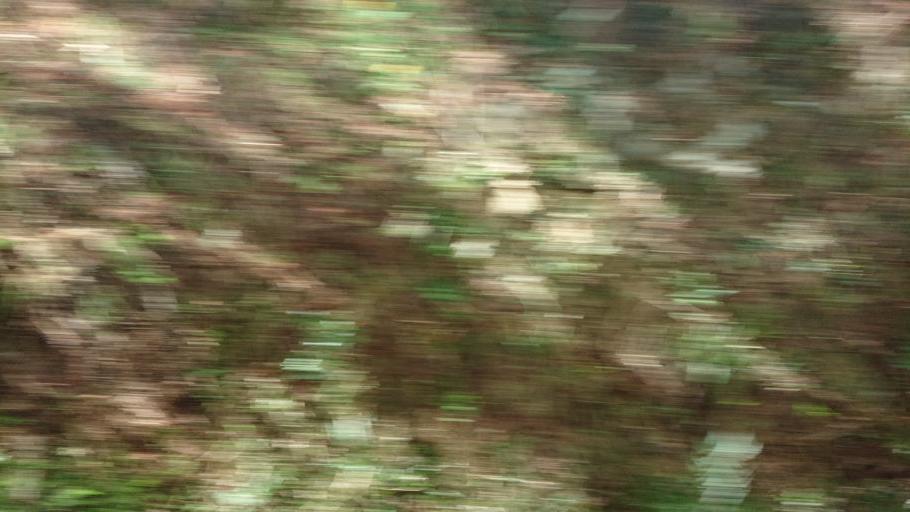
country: TW
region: Taiwan
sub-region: Hualien
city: Hualian
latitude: 24.3459
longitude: 121.3100
